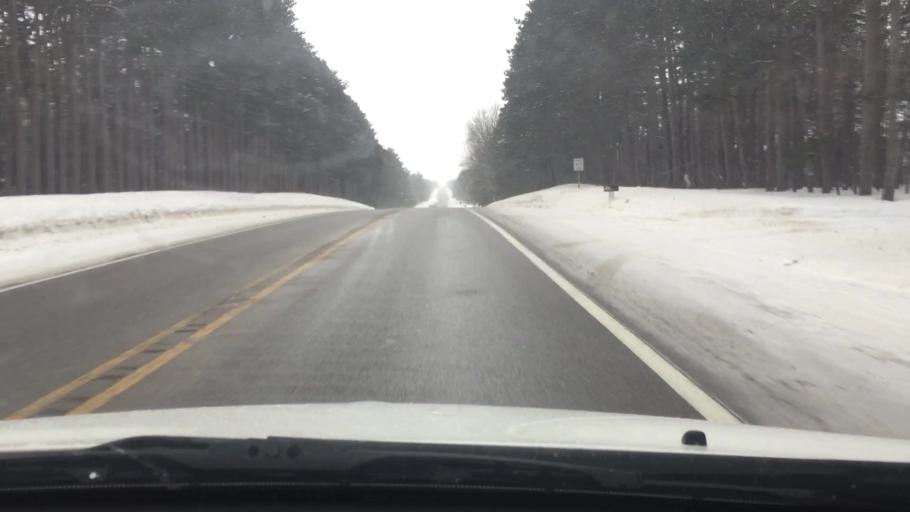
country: US
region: Michigan
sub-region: Otsego County
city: Gaylord
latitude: 45.0618
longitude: -84.8097
